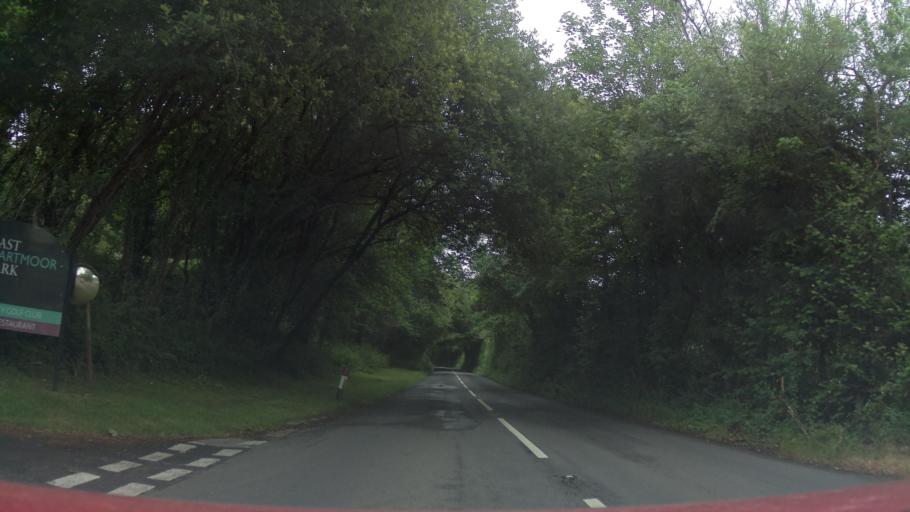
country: GB
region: England
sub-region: Devon
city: Chudleigh
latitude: 50.6382
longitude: -3.6383
